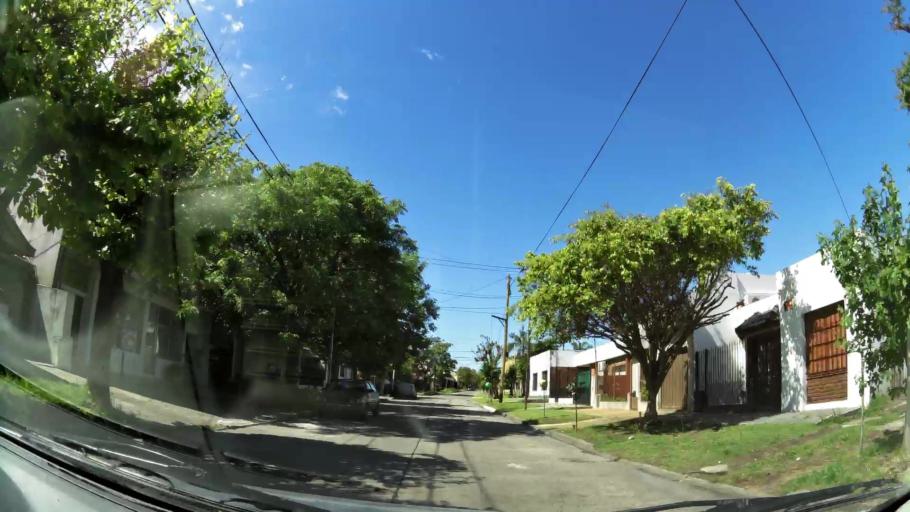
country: AR
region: Buenos Aires
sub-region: Partido de Quilmes
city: Quilmes
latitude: -34.6980
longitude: -58.3028
